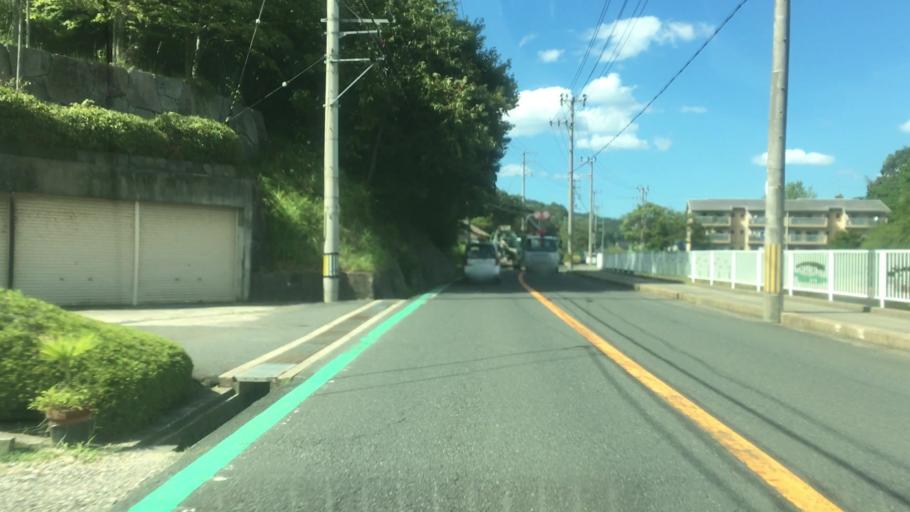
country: JP
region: Kyoto
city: Miyazu
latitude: 35.6140
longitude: 135.0540
